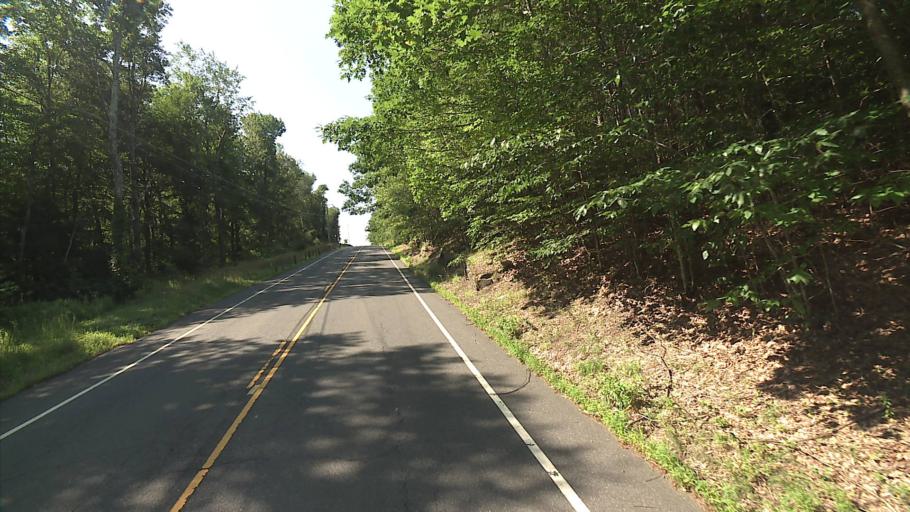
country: US
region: Massachusetts
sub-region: Hampden County
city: Granville
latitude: 42.0228
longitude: -72.9672
